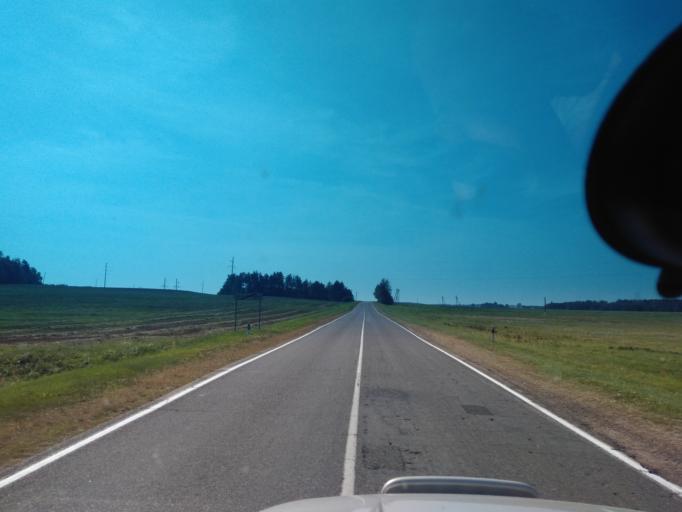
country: BY
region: Minsk
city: Uzda
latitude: 53.3858
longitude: 27.2427
